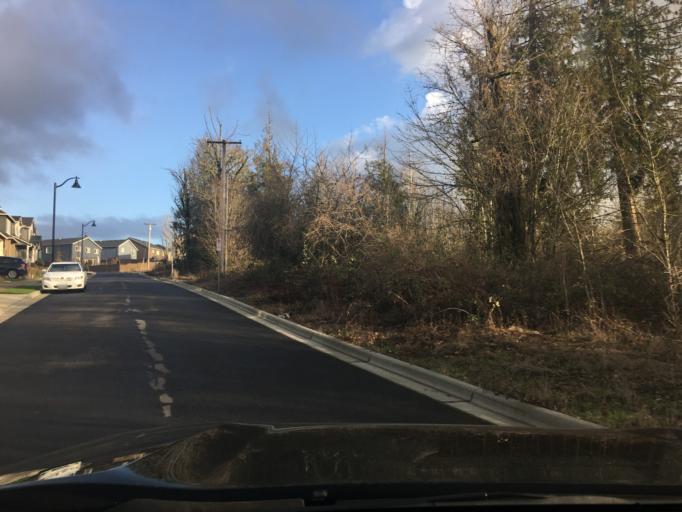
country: US
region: Oregon
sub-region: Washington County
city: Bethany
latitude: 45.5740
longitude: -122.8568
